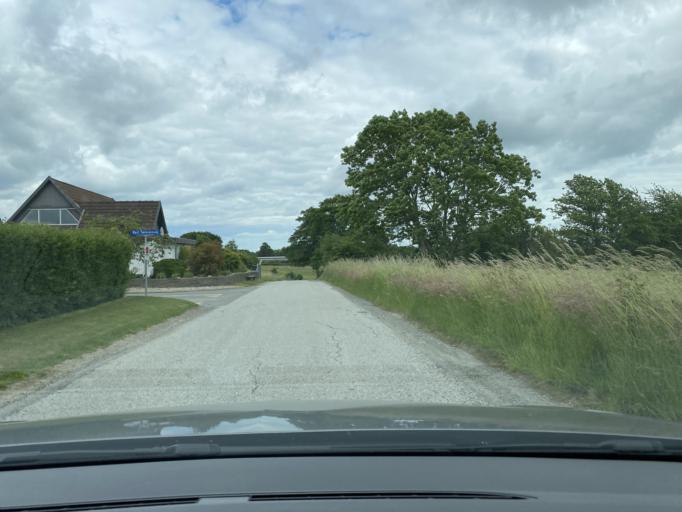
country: DK
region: South Denmark
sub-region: Vejle Kommune
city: Brejning
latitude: 55.6365
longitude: 9.7218
